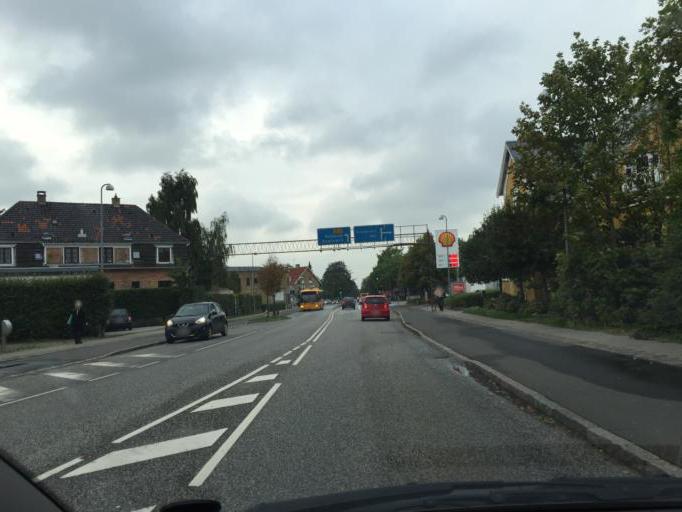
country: DK
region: Capital Region
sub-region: Gladsaxe Municipality
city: Buddinge
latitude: 55.7649
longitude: 12.4896
